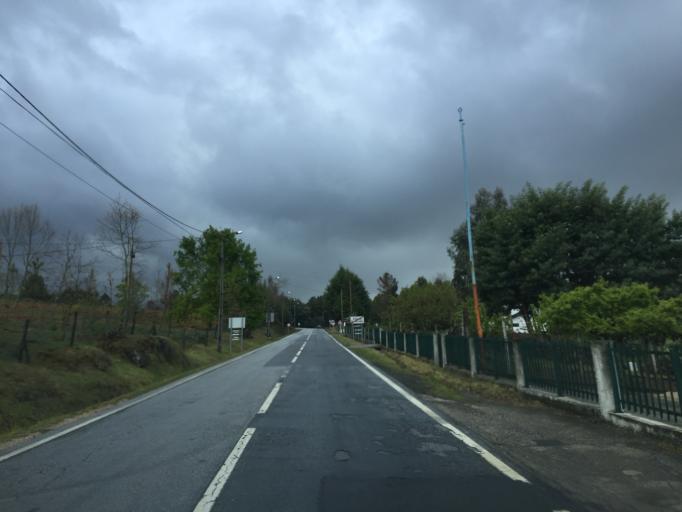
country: PT
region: Guarda
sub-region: Seia
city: Seia
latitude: 40.3961
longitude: -7.7427
